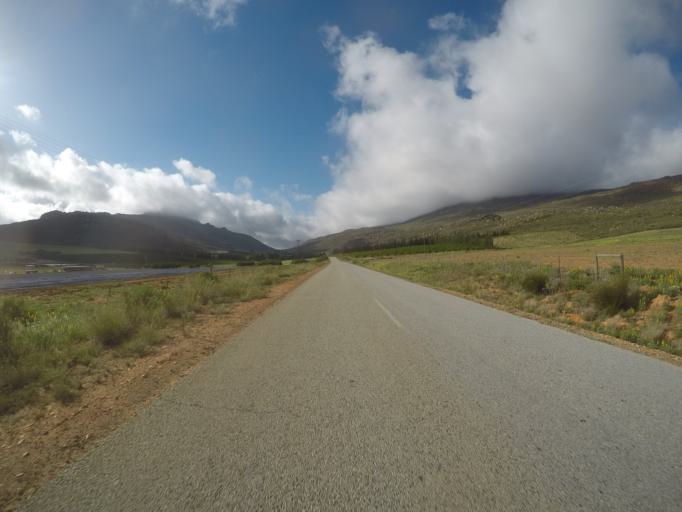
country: ZA
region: Western Cape
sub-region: West Coast District Municipality
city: Clanwilliam
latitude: -32.3534
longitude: 18.8496
